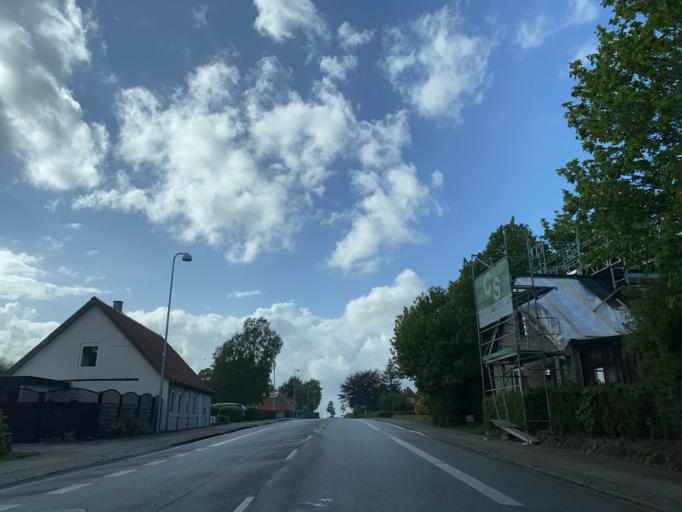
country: DK
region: Central Jutland
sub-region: Horsens Kommune
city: Horsens
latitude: 55.8925
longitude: 9.7721
